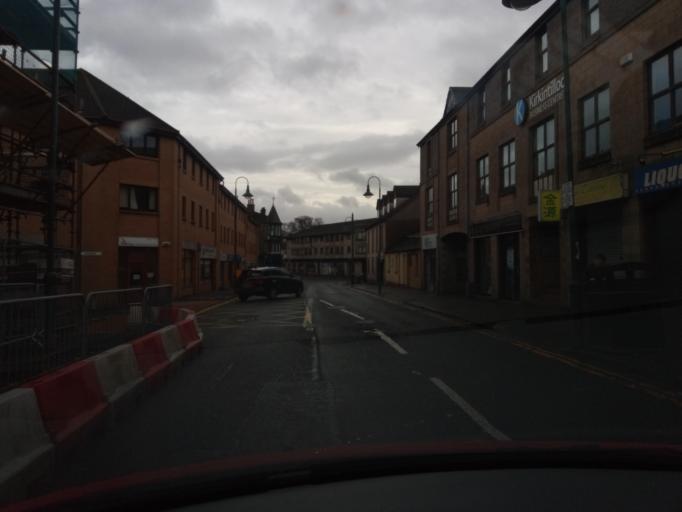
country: GB
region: Scotland
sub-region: East Dunbartonshire
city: Kirkintilloch
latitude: 55.9364
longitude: -4.1528
